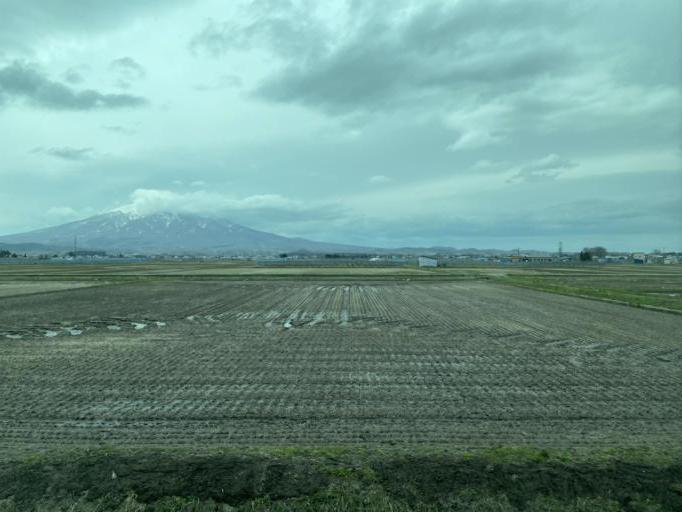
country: JP
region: Aomori
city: Goshogawara
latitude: 40.7329
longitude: 140.4387
